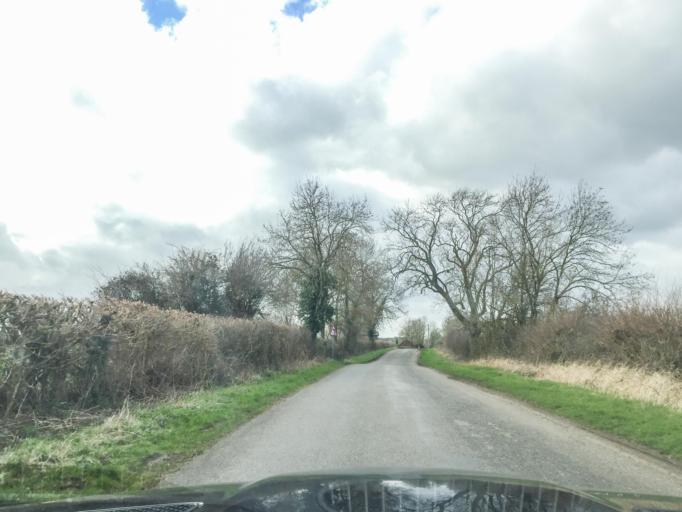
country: GB
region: England
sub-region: Warwickshire
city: Shipston on Stour
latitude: 52.0623
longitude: -1.5513
